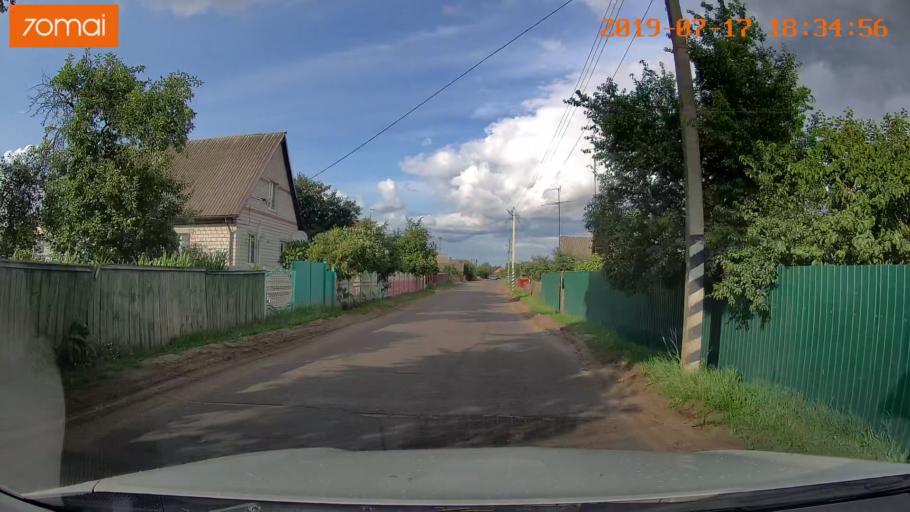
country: BY
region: Mogilev
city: Asipovichy
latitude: 53.2900
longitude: 28.6535
